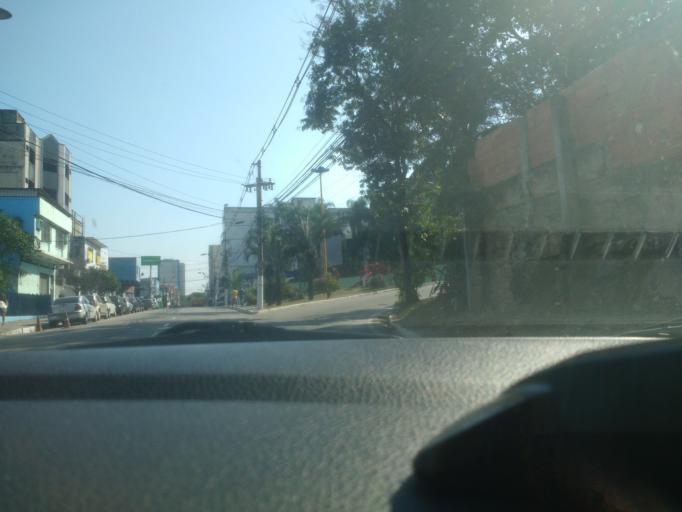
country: BR
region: Rio de Janeiro
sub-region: Duque De Caxias
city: Duque de Caxias
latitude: -22.8007
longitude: -43.2923
